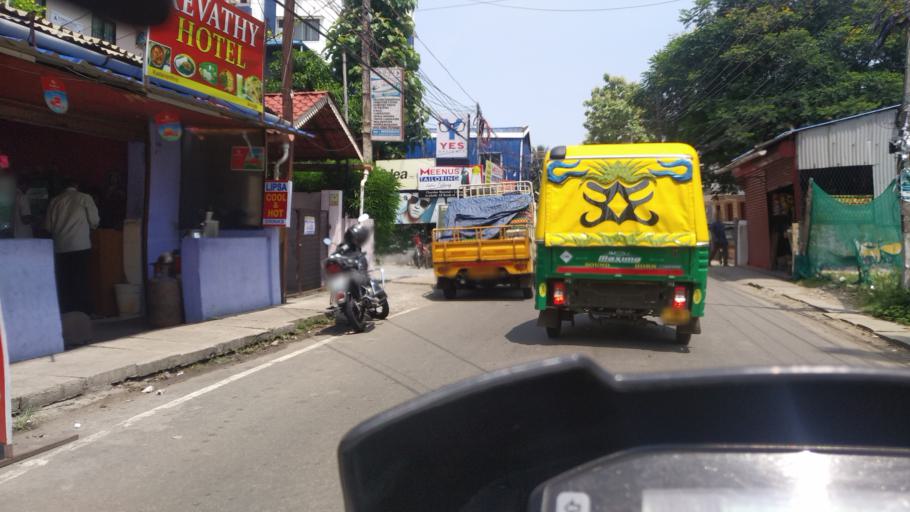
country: IN
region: Kerala
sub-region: Ernakulam
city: Cochin
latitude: 9.9532
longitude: 76.3024
